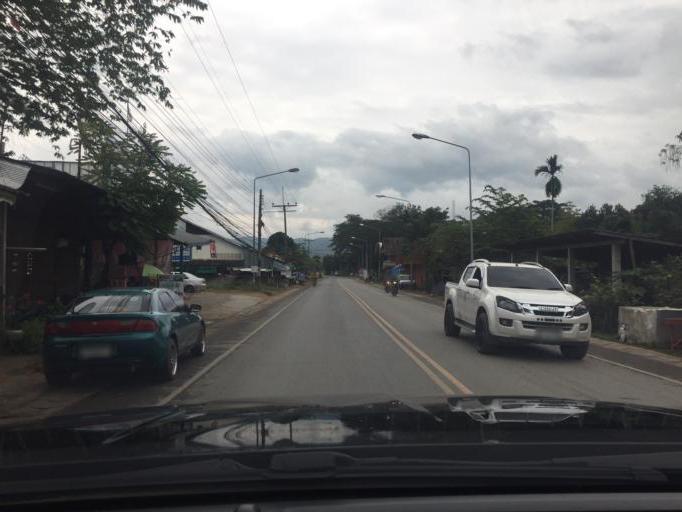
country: TH
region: Phayao
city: Pong
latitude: 19.1702
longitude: 100.2832
